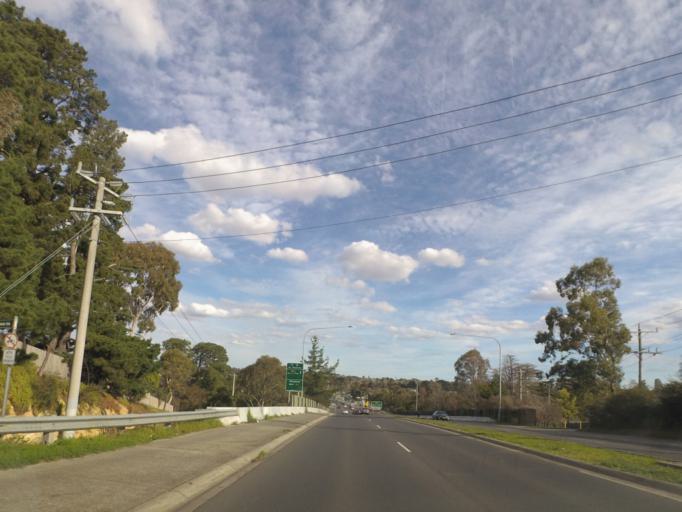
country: AU
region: Victoria
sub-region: Manningham
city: Doncaster East
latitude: -37.7952
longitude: 145.1424
